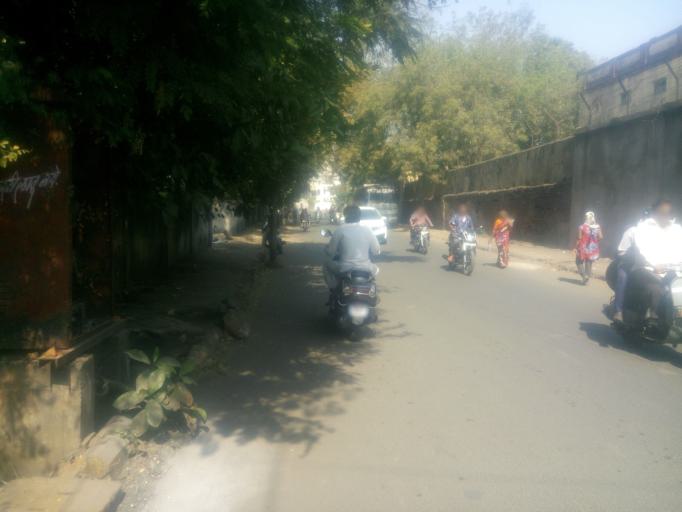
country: IN
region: Maharashtra
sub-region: Nagpur Division
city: Nagpur
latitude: 21.1615
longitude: 79.0818
